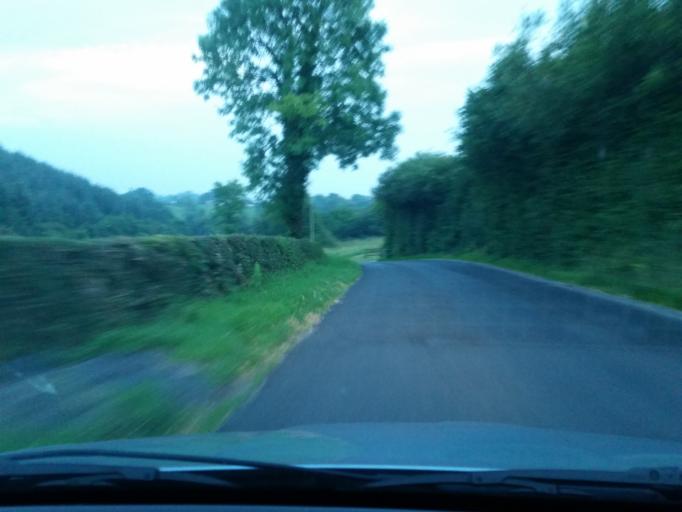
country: IE
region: Ulster
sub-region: County Monaghan
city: Clones
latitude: 54.2410
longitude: -7.2651
